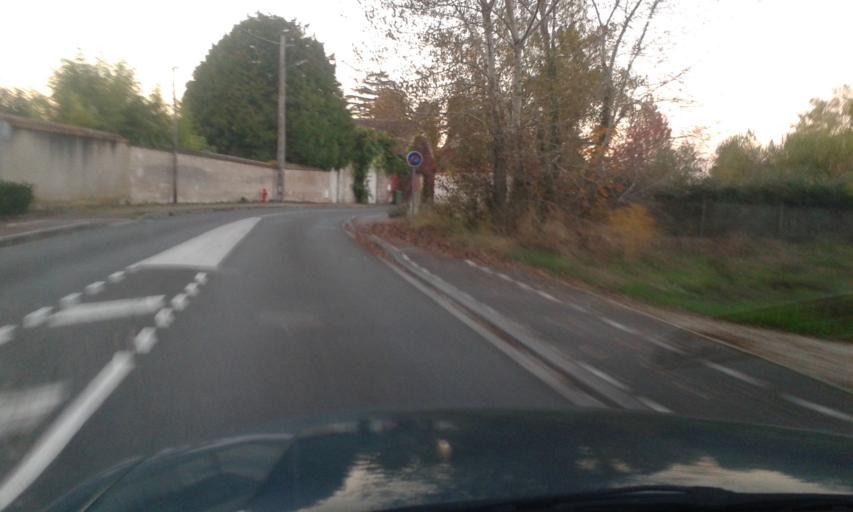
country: FR
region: Centre
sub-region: Departement du Loiret
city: Olivet
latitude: 47.8567
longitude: 1.8817
